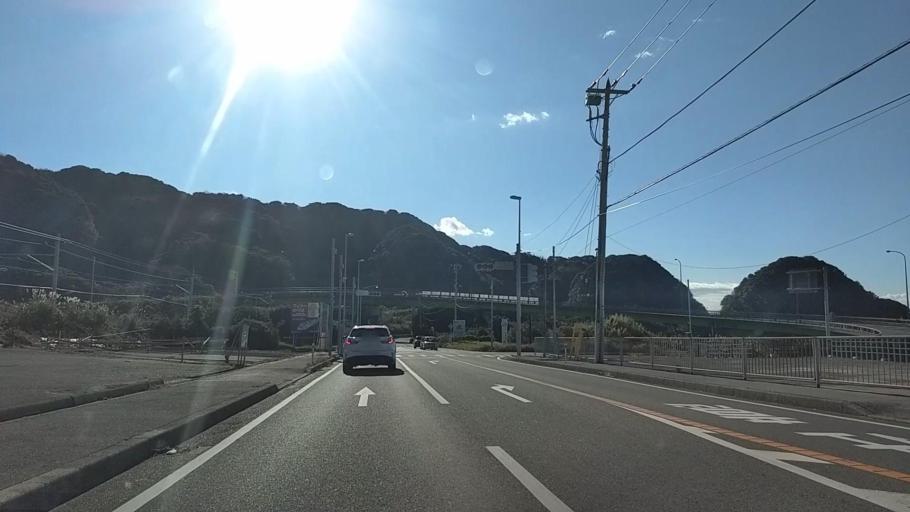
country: JP
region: Chiba
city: Futtsu
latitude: 35.1754
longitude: 139.8187
